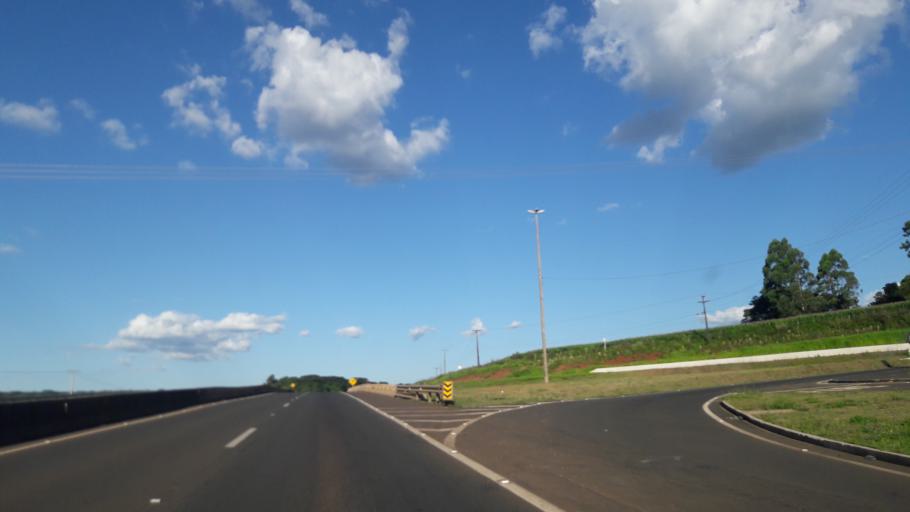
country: BR
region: Parana
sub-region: Guarapuava
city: Guarapuava
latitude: -25.3406
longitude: -51.4312
